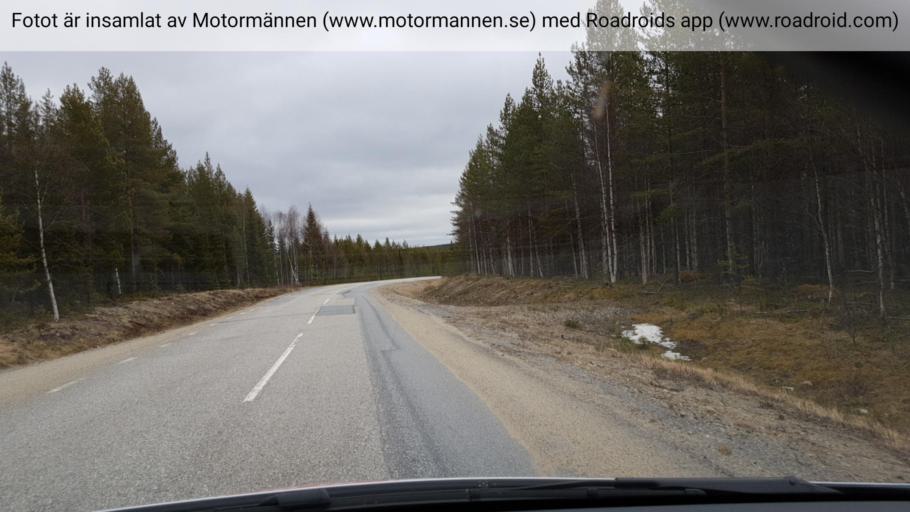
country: SE
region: Vaesterbotten
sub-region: Lycksele Kommun
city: Lycksele
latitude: 64.0448
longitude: 18.4368
